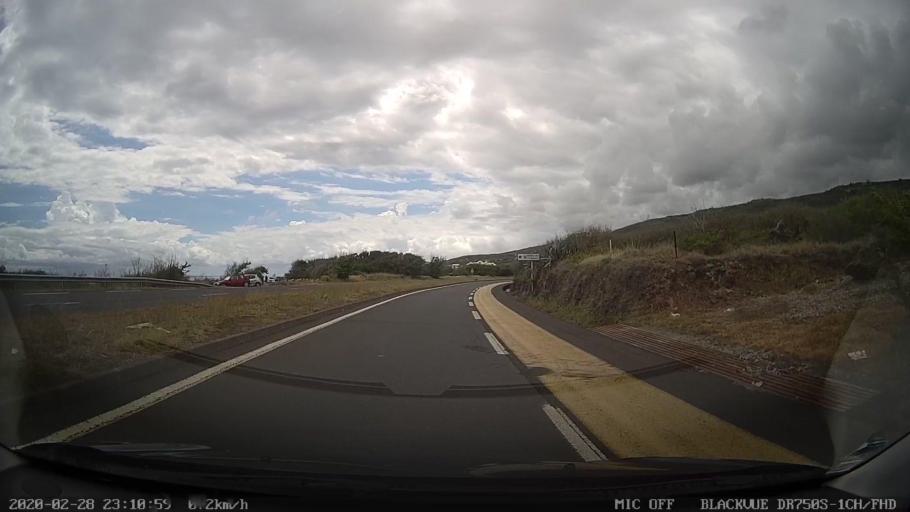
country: RE
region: Reunion
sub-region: Reunion
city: Trois-Bassins
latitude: -21.1143
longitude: 55.2565
